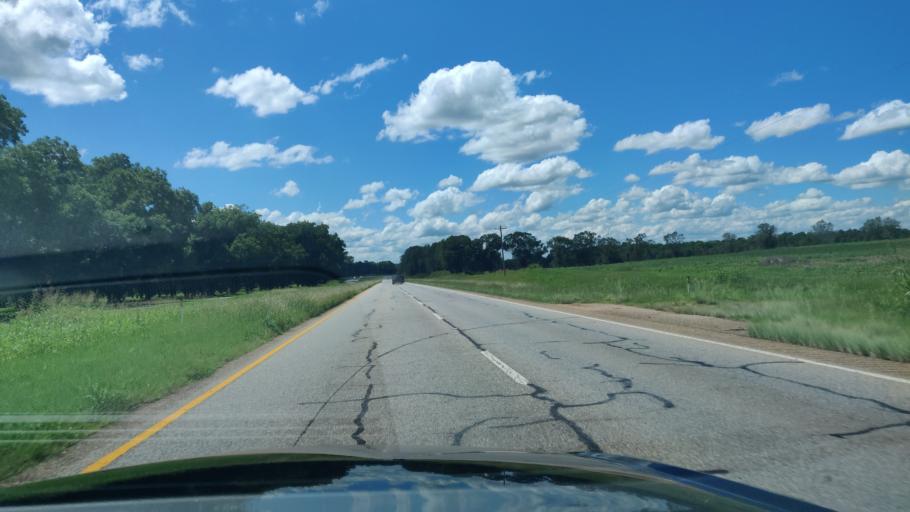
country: US
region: Georgia
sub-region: Stewart County
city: Richland
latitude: 31.9953
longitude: -84.6397
